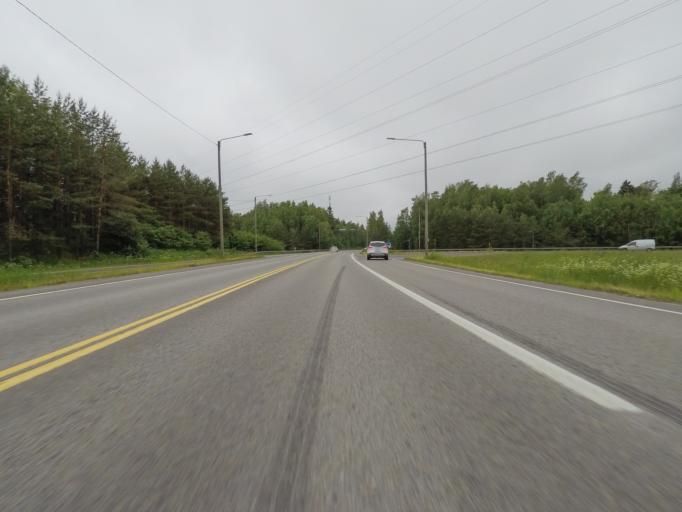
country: FI
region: Varsinais-Suomi
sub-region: Turku
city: Raisio
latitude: 60.4645
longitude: 22.1045
